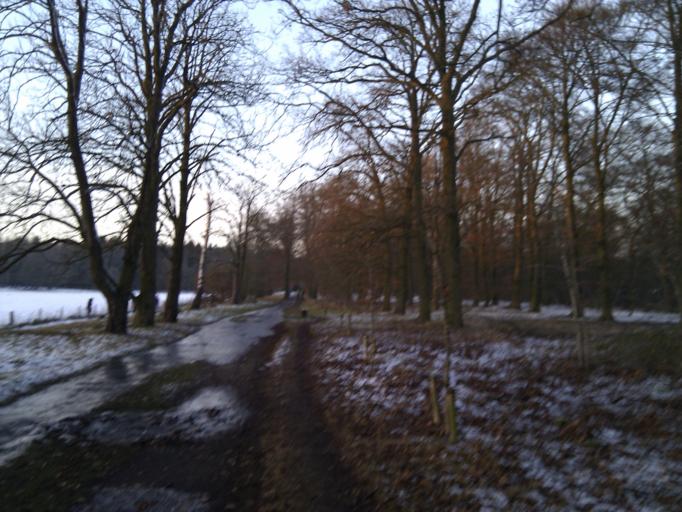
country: NL
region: Utrecht
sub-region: Gemeente De Bilt
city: De Bilt
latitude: 52.1139
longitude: 5.2014
